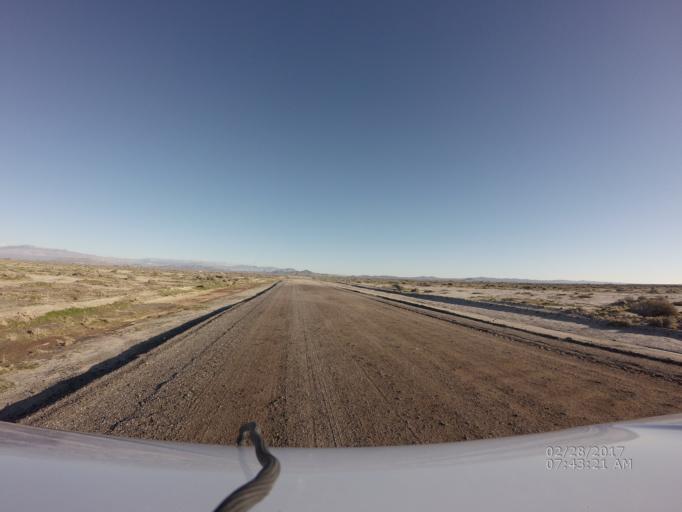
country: US
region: California
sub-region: Kern County
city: Rosamond
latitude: 34.7893
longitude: -118.1848
